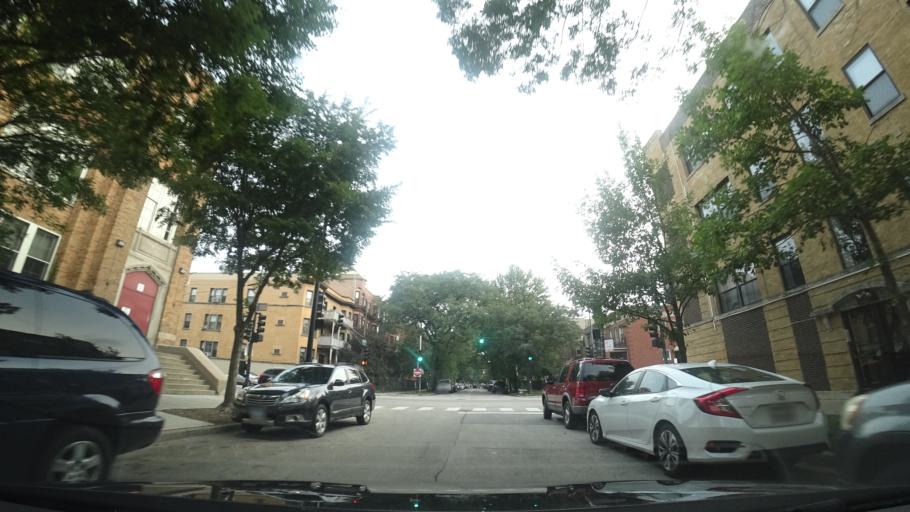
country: US
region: Illinois
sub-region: Cook County
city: Evanston
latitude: 41.9761
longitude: -87.6578
